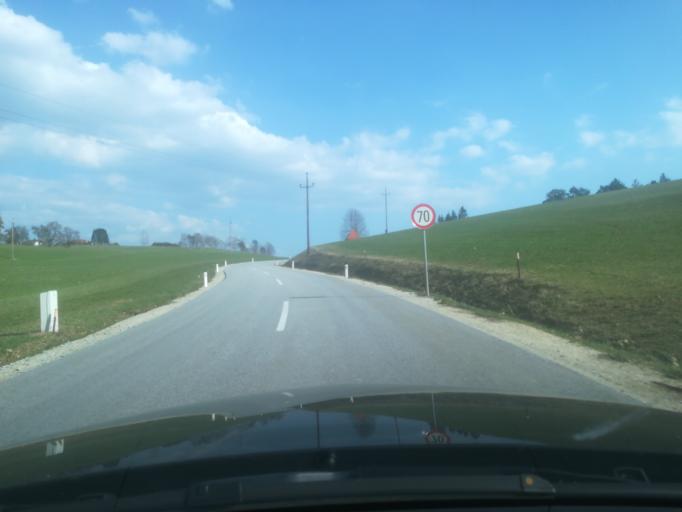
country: AT
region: Upper Austria
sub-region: Politischer Bezirk Perg
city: Perg
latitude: 48.3613
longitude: 14.6560
